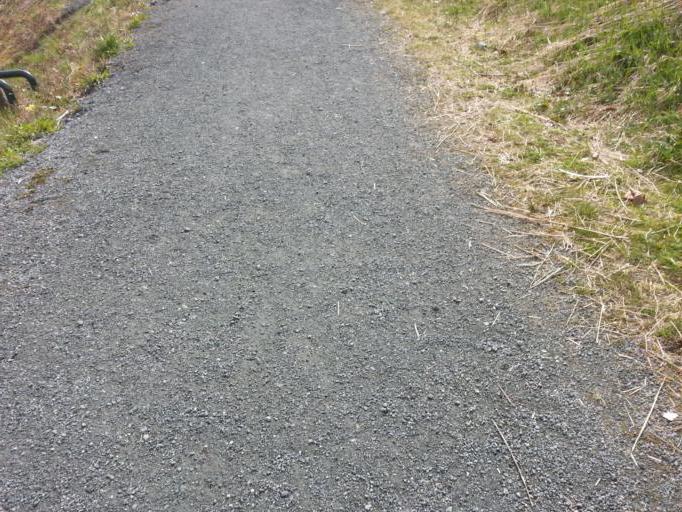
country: NO
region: Sor-Trondelag
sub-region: Trondheim
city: Trondheim
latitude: 63.3939
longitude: 10.3439
